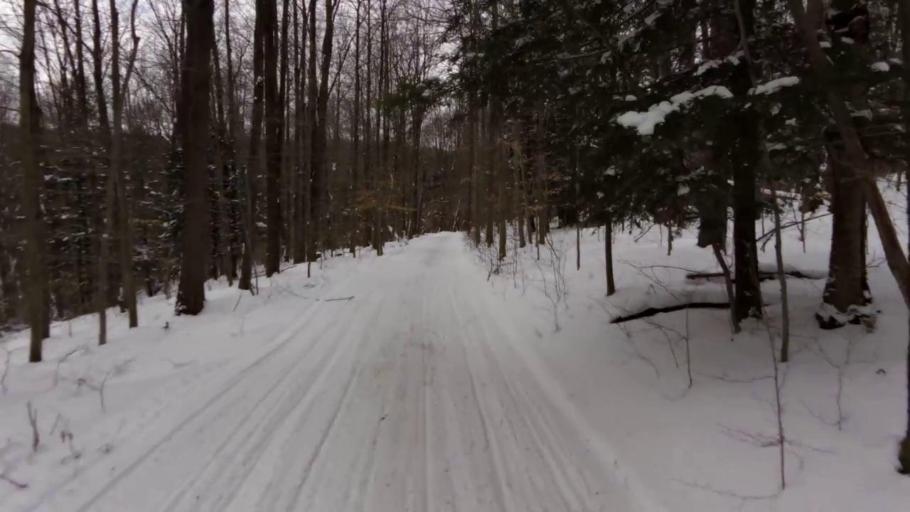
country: US
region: Pennsylvania
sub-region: McKean County
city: Bradford
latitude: 42.0122
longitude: -78.7253
